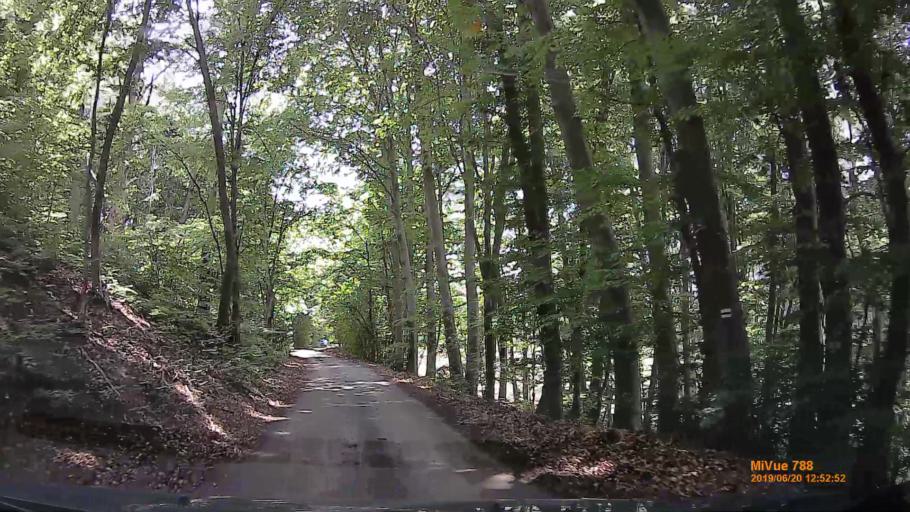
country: HU
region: Baranya
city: Hosszuheteny
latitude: 46.2133
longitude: 18.3616
